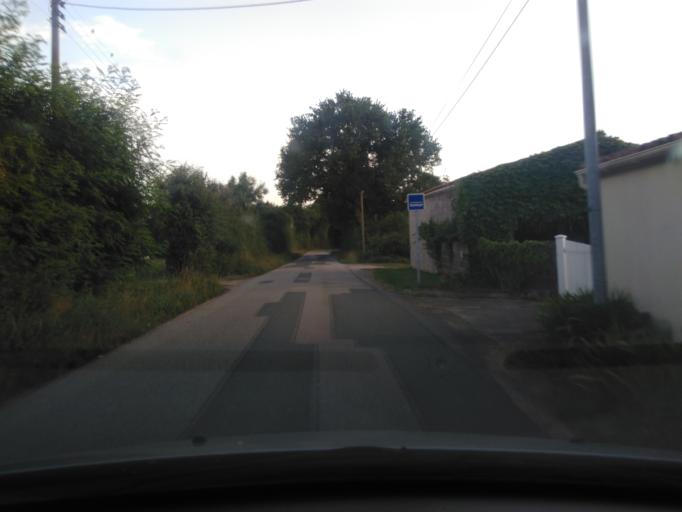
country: FR
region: Pays de la Loire
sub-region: Departement de la Vendee
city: Saint-Florent-des-Bois
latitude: 46.6018
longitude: -1.3578
